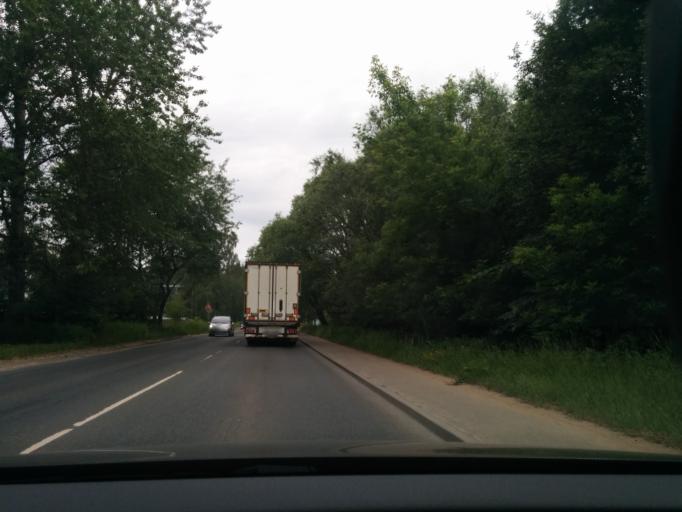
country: LV
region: Kekava
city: Balozi
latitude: 56.9153
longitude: 24.2003
